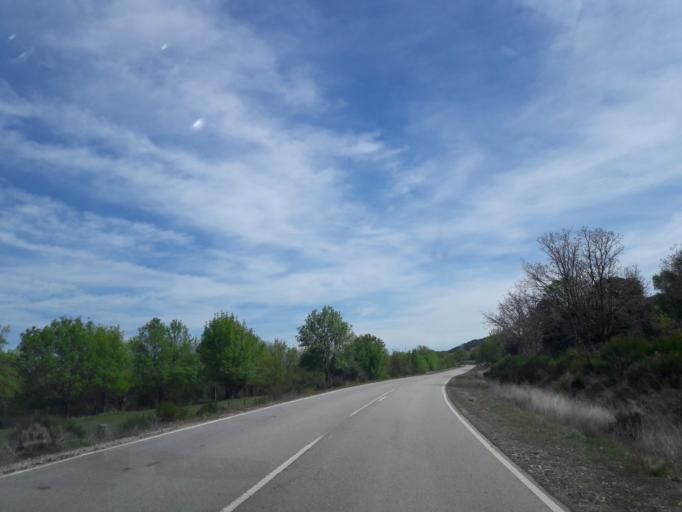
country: ES
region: Castille and Leon
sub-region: Provincia de Salamanca
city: Ledrada
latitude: 40.4533
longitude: -5.7347
